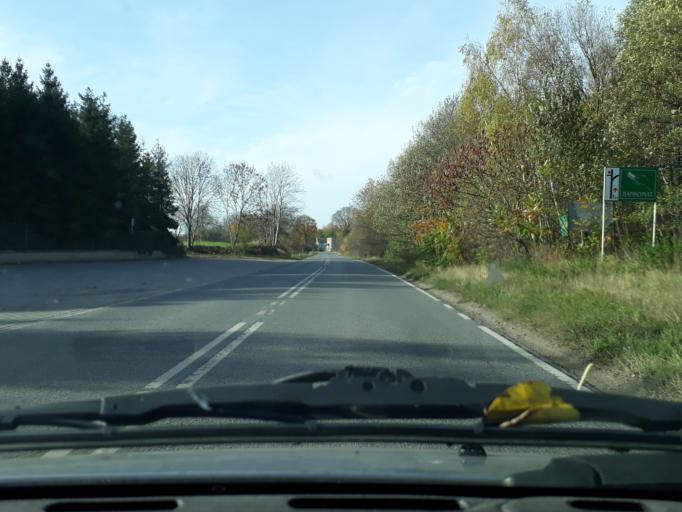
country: PL
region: Silesian Voivodeship
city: Wozniki
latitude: 50.5914
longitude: 19.0744
